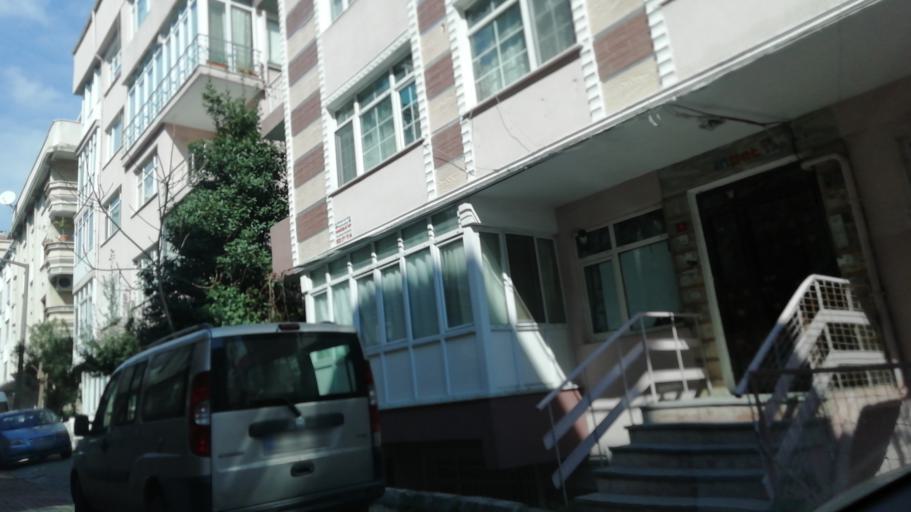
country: TR
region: Istanbul
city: Yakuplu
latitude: 40.9737
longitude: 28.7325
